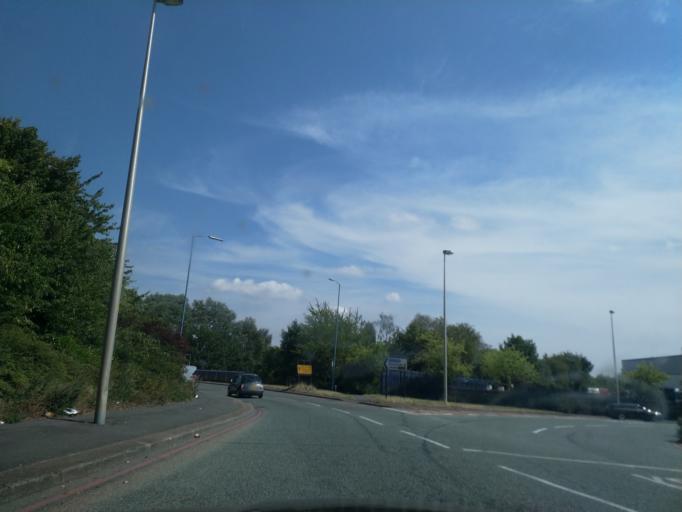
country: GB
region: England
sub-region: Sandwell
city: Smethwick
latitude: 52.5070
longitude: -1.9763
